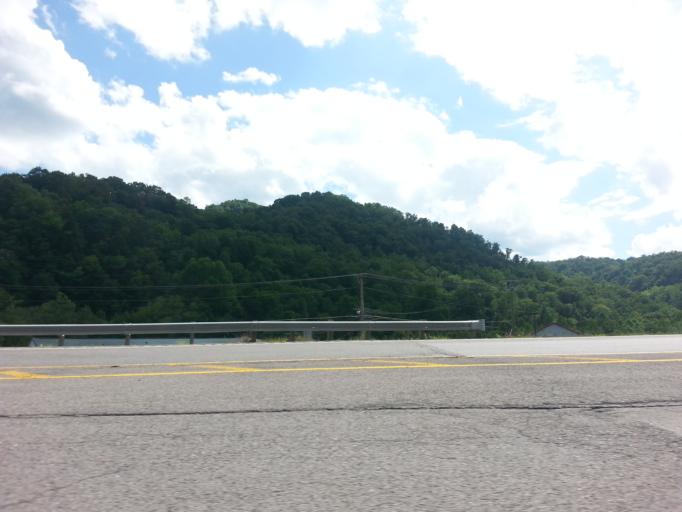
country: US
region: Kentucky
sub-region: Harlan County
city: Harlan
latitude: 36.8083
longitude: -83.3096
